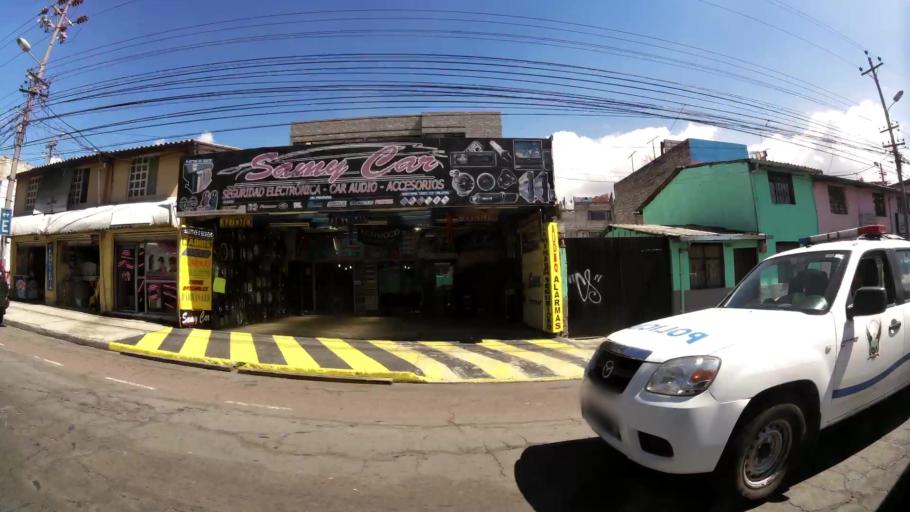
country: EC
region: Pichincha
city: Quito
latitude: -0.2579
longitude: -78.5342
